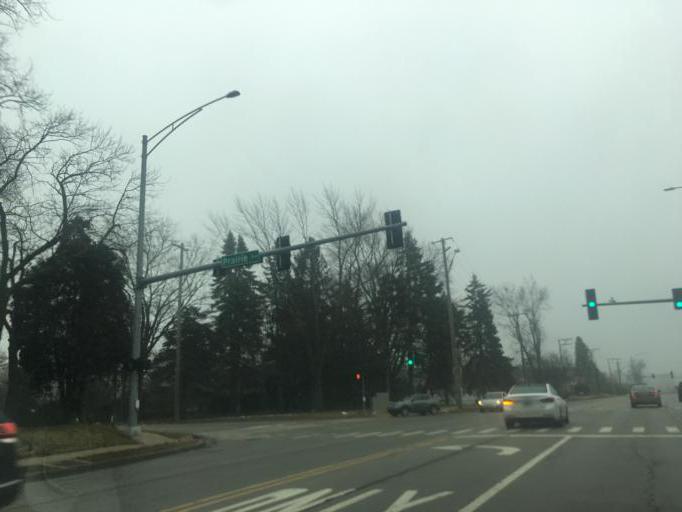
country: US
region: Illinois
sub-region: DuPage County
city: Downers Grove
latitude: 41.7997
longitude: -88.0373
